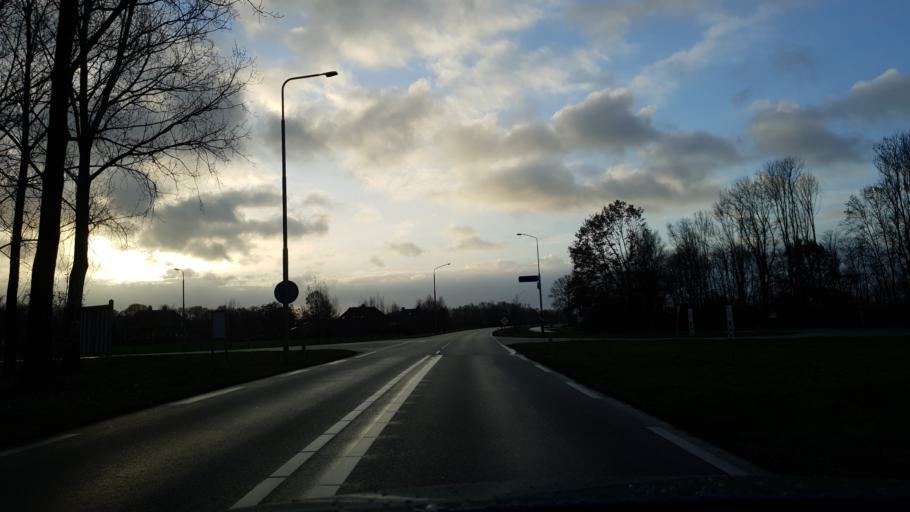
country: NL
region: Gelderland
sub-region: Gemeente Wijchen
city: Wijchen
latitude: 51.8200
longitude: 5.6902
